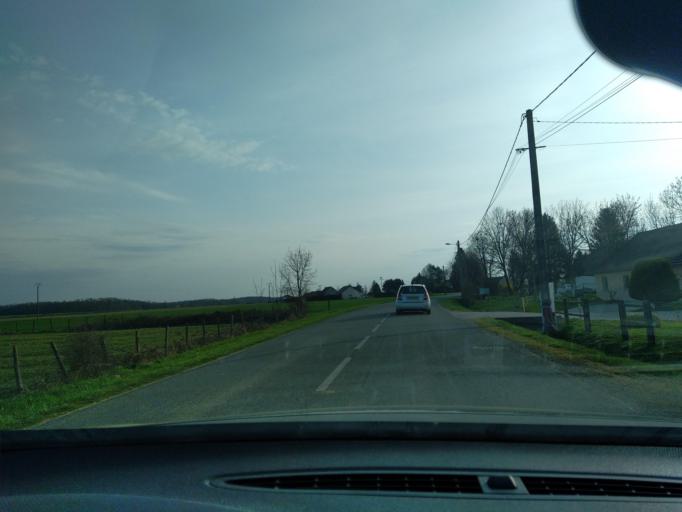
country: FR
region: Franche-Comte
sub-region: Departement du Jura
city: Chaussin
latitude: 46.9784
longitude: 5.4283
